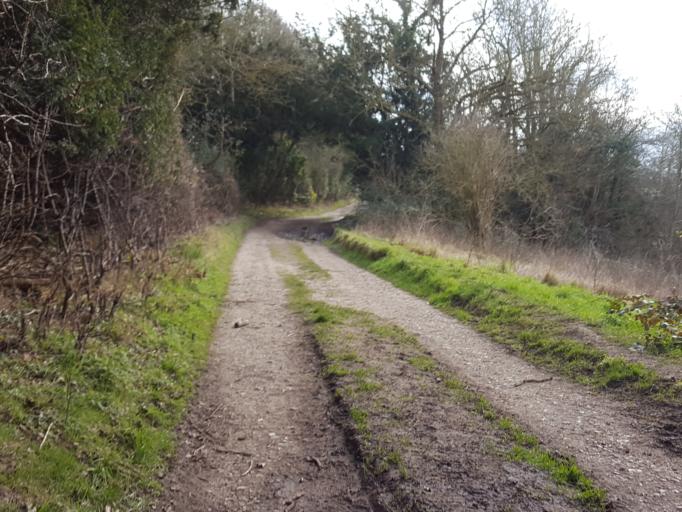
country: GB
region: England
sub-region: Buckinghamshire
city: High Wycombe
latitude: 51.6508
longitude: -0.8080
